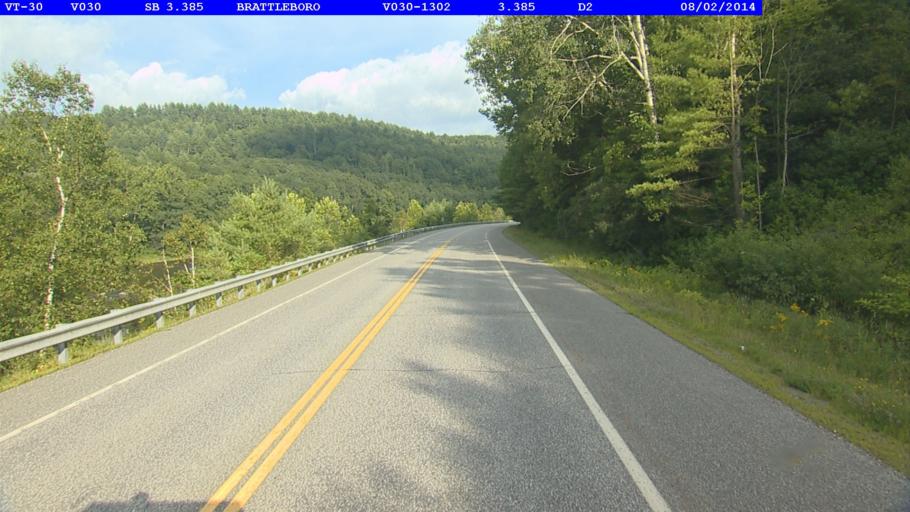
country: US
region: Vermont
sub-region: Windham County
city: West Brattleboro
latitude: 42.8959
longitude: -72.5952
